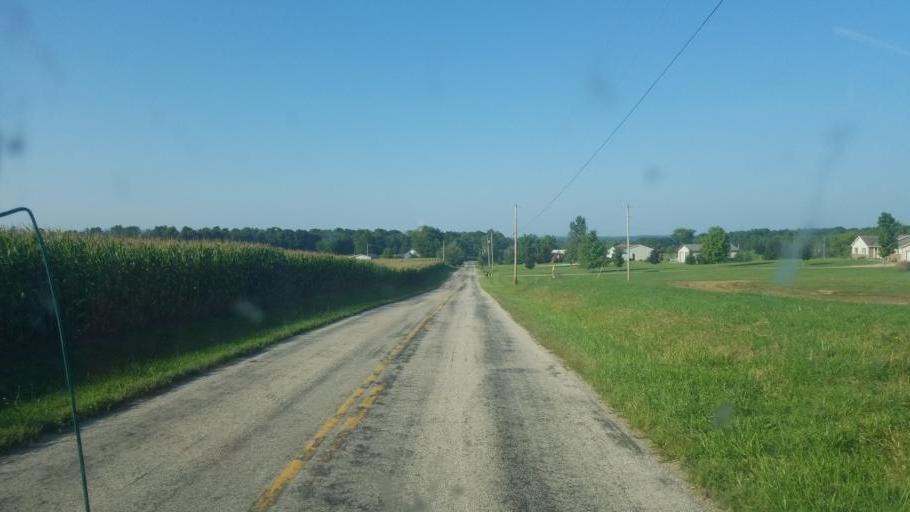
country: US
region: Ohio
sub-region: Ashland County
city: Ashland
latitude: 40.9800
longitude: -82.3444
